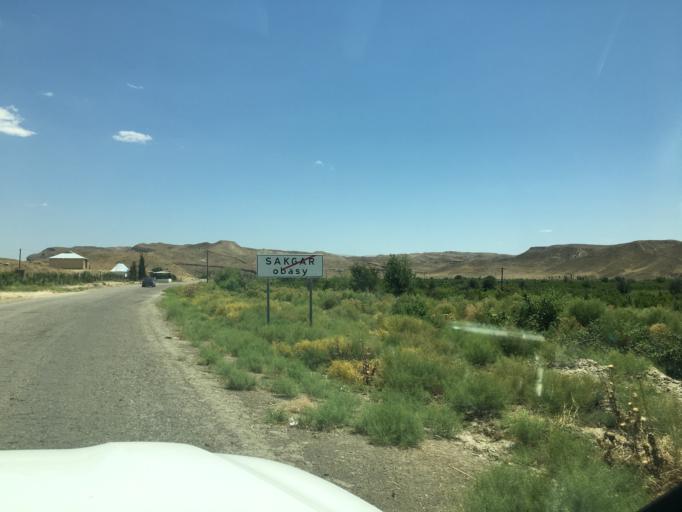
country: TM
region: Balkan
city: Magtymguly
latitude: 38.4295
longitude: 56.4082
